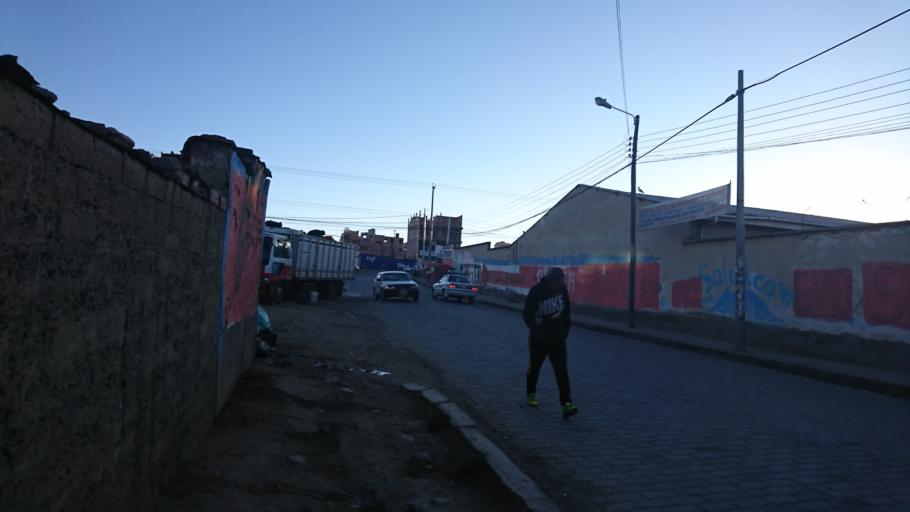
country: BO
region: La Paz
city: La Paz
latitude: -16.4971
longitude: -68.1880
